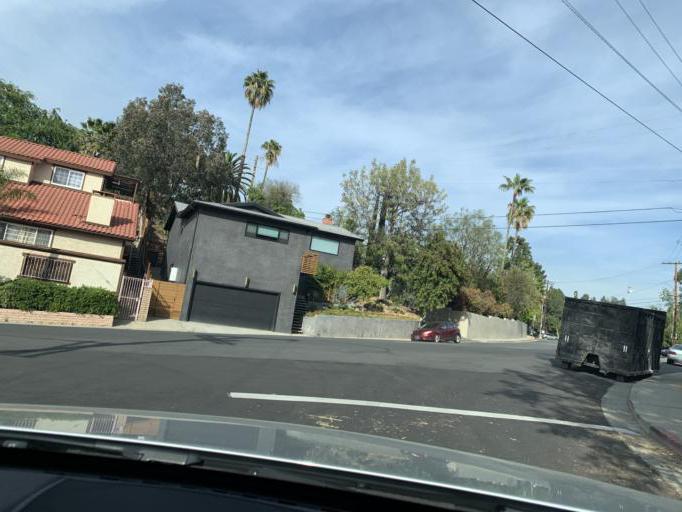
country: US
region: California
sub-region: Los Angeles County
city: Pasadena
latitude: 34.1420
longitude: -118.1904
